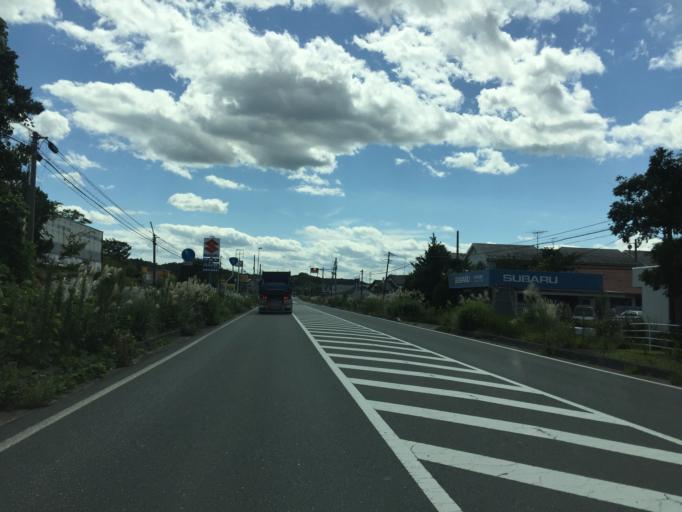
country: JP
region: Fukushima
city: Namie
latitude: 37.4508
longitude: 141.0092
